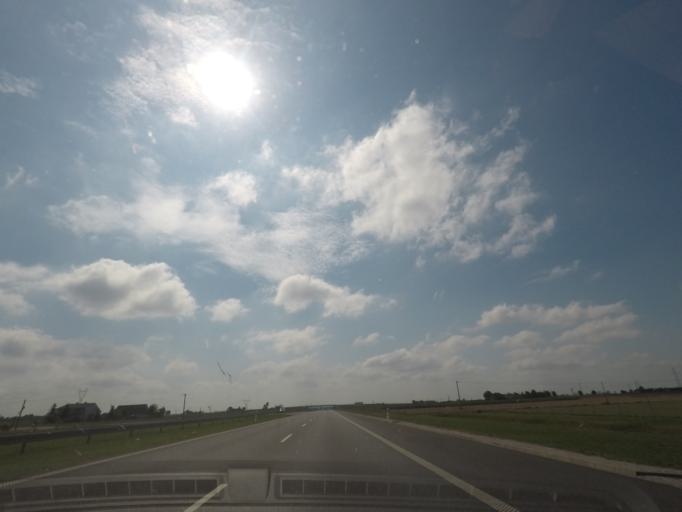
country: PL
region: Kujawsko-Pomorskie
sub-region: Powiat wloclawski
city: Lubanie
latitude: 52.7189
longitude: 18.8704
